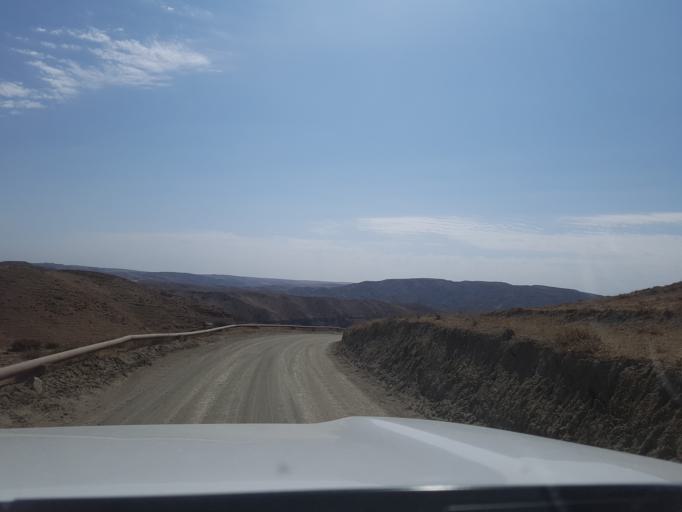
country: TM
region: Ahal
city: Baharly
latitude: 38.2419
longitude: 56.8899
